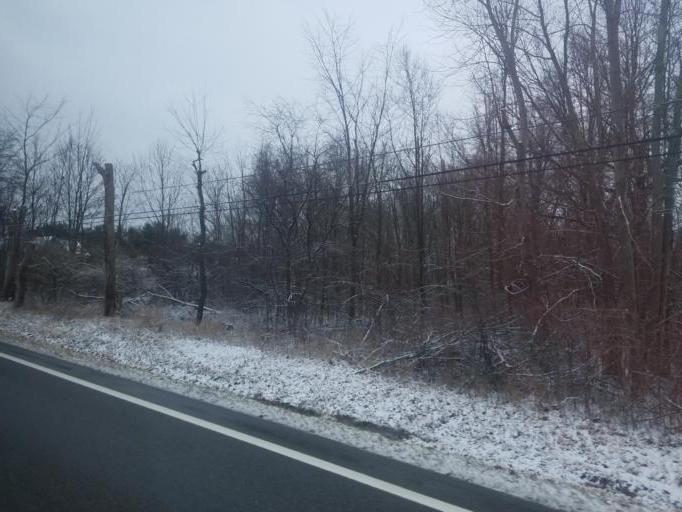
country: US
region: Ohio
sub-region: Licking County
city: Johnstown
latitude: 40.1833
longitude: -82.7473
